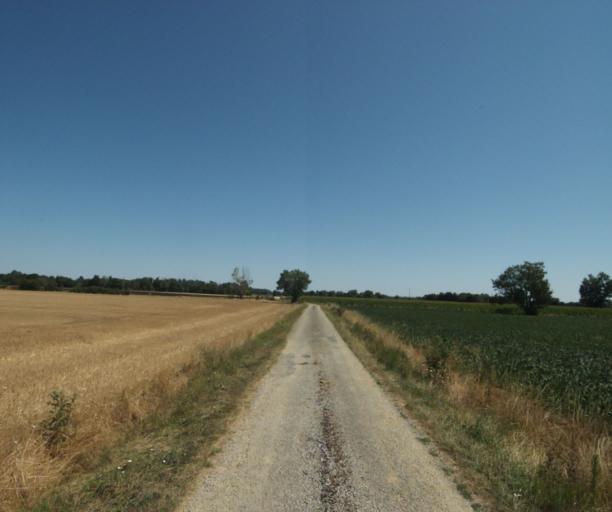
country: FR
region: Midi-Pyrenees
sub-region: Departement de la Haute-Garonne
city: Revel
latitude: 43.4839
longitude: 1.9561
